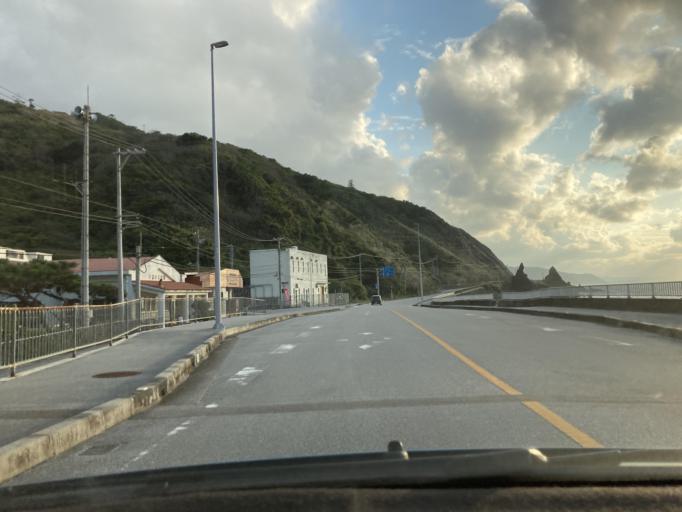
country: JP
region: Okinawa
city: Nago
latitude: 26.8089
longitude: 128.2342
